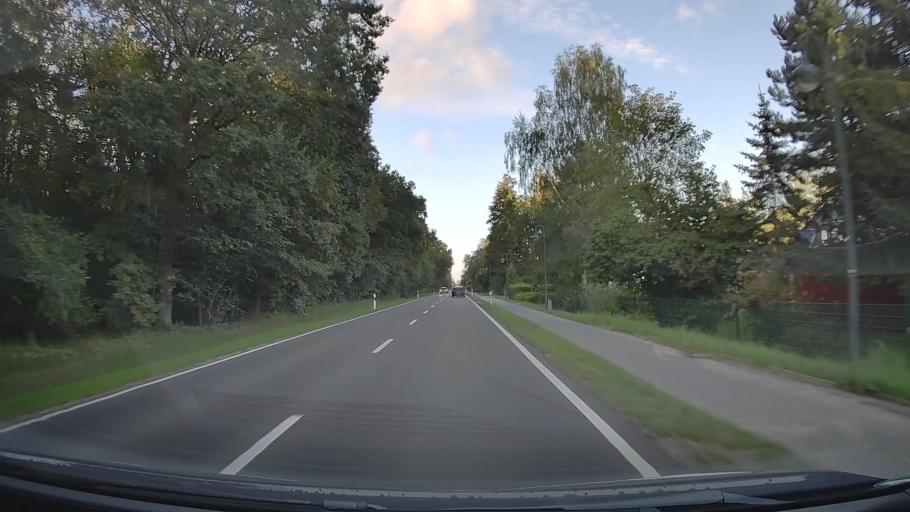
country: DE
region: Mecklenburg-Vorpommern
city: Steinhagen
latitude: 54.2471
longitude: 13.0202
